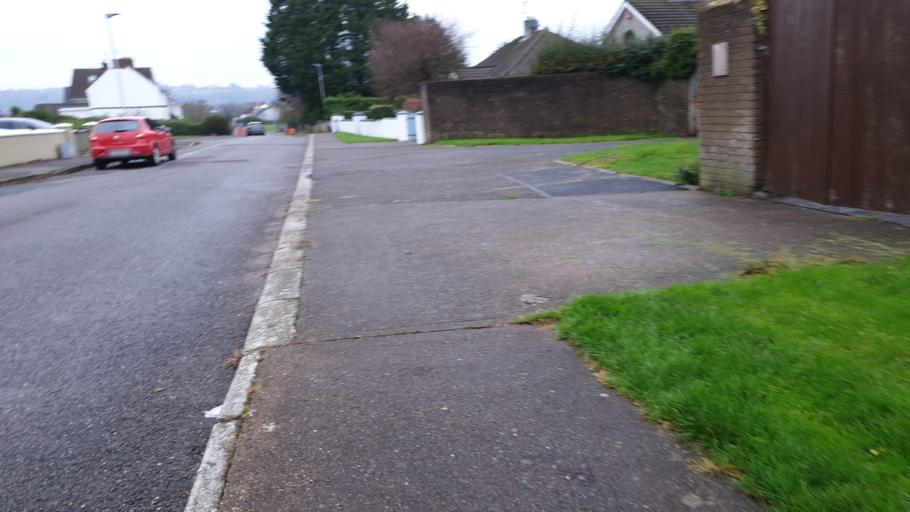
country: IE
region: Munster
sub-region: County Cork
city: Cork
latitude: 51.8914
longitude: -8.4070
